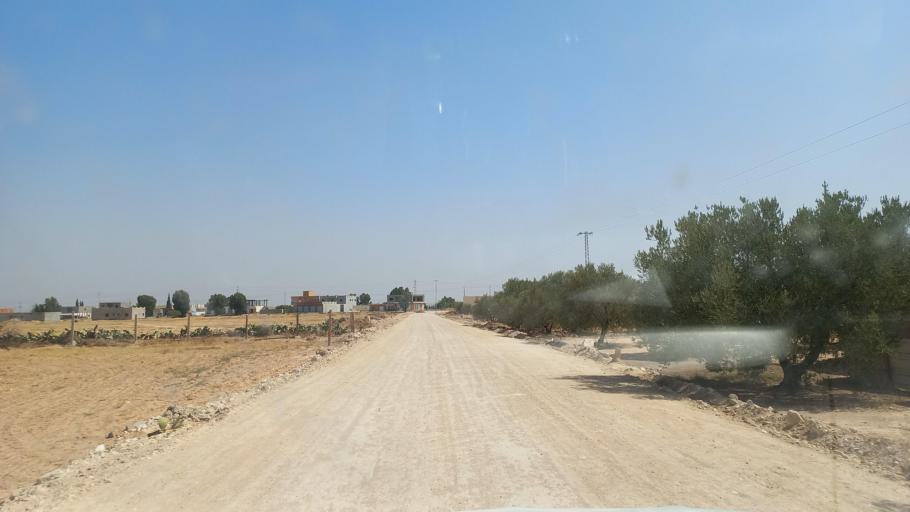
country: TN
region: Al Qasrayn
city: Kasserine
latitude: 35.2559
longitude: 9.0148
